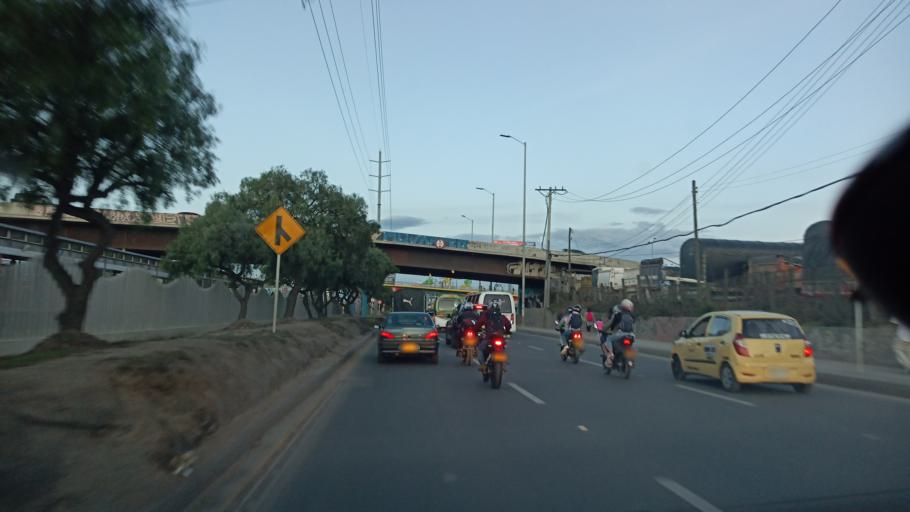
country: CO
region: Cundinamarca
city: Soacha
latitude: 4.5864
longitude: -74.2044
